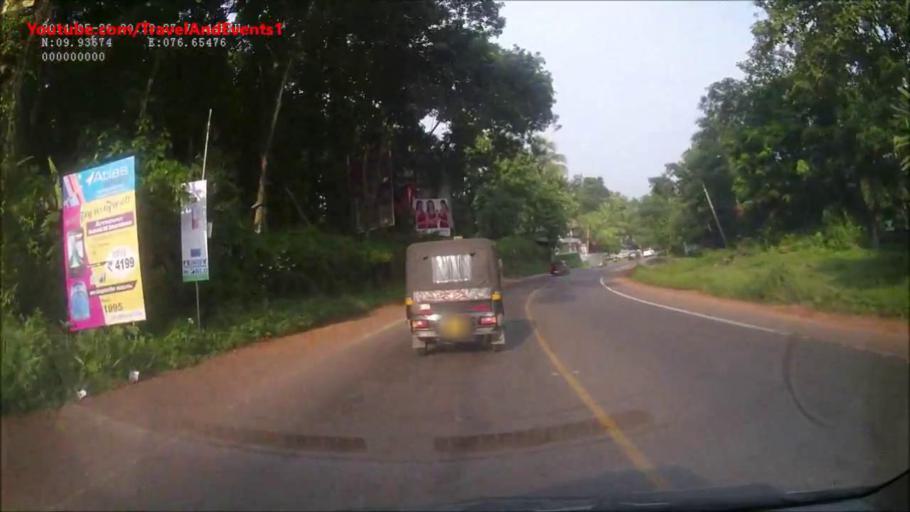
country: IN
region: Kerala
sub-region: Ernakulam
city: Muvattupula
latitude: 9.9329
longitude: 76.6612
